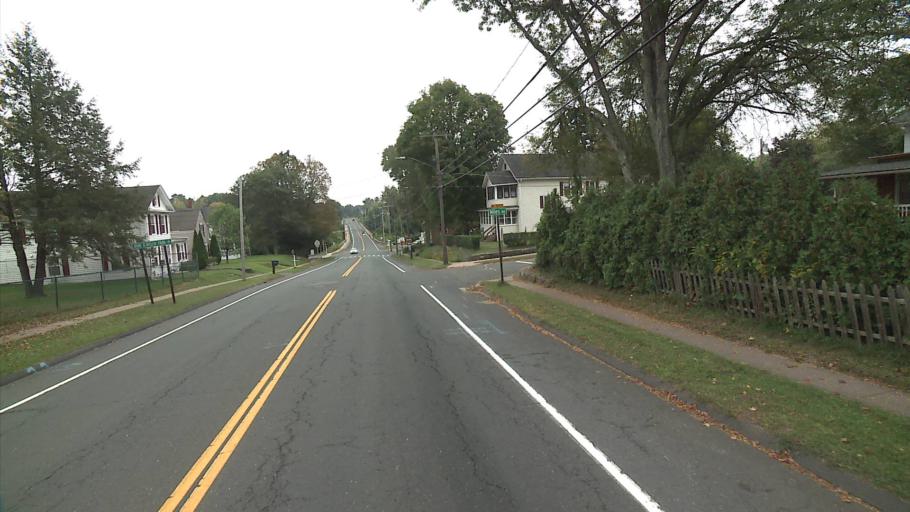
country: US
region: Connecticut
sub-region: Hartford County
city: Windsor Locks
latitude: 41.9032
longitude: -72.6792
